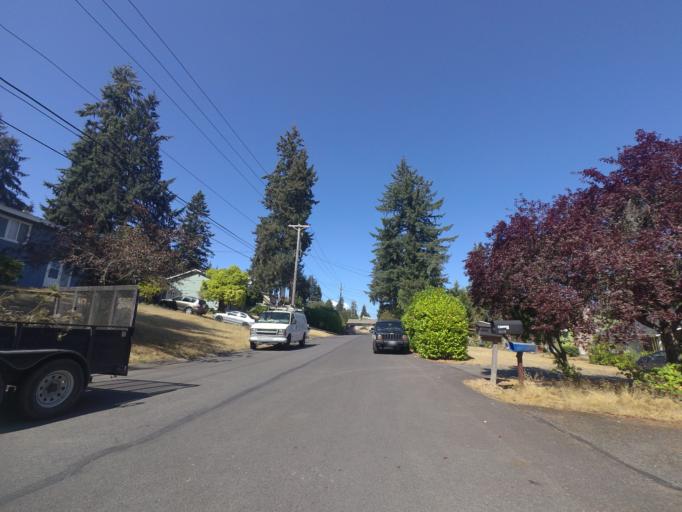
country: US
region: Washington
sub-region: Pierce County
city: Fircrest
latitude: 47.2197
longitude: -122.5123
